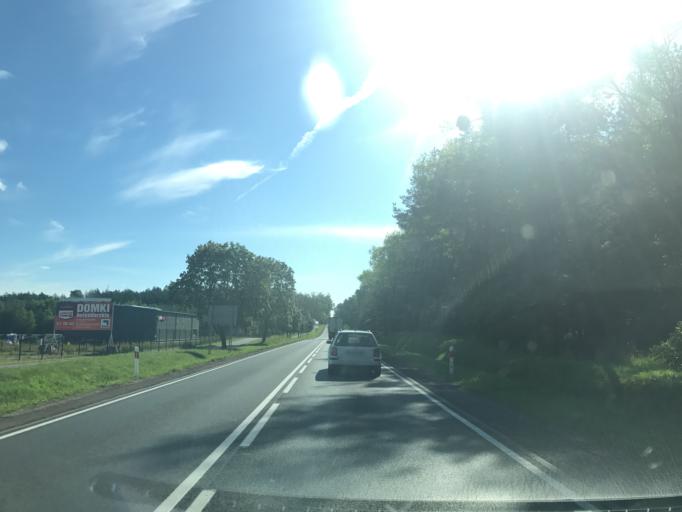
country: PL
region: Pomeranian Voivodeship
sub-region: Powiat czluchowski
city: Czluchow
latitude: 53.6855
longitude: 17.4347
